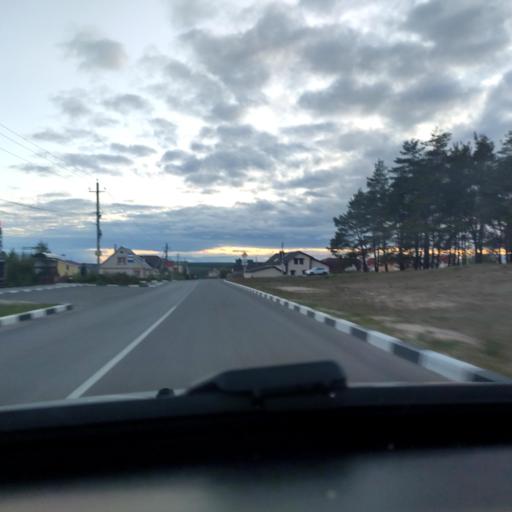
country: RU
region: Voronezj
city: Kolodeznyy
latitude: 51.3262
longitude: 39.2006
